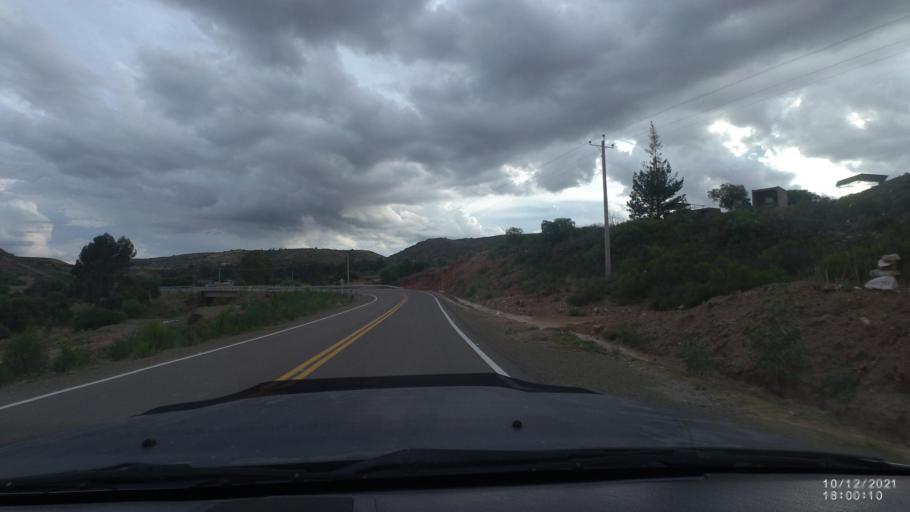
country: BO
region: Cochabamba
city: Cliza
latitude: -17.7396
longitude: -65.9223
